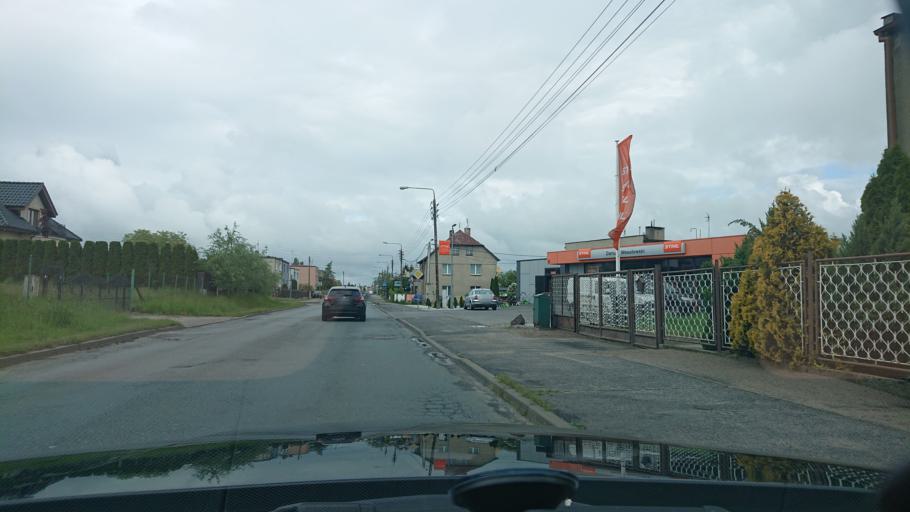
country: PL
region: Greater Poland Voivodeship
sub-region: Powiat gnieznienski
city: Gniezno
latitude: 52.5119
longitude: 17.6017
